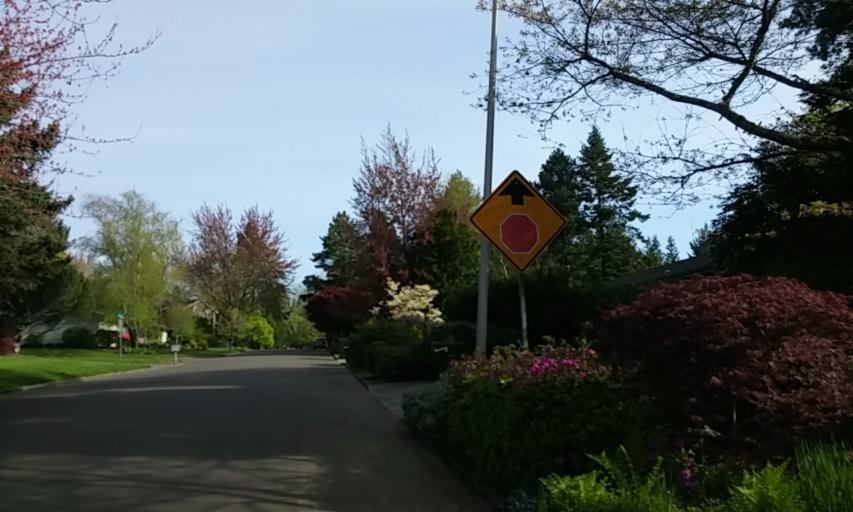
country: US
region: Oregon
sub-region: Washington County
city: West Slope
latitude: 45.5023
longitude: -122.7707
